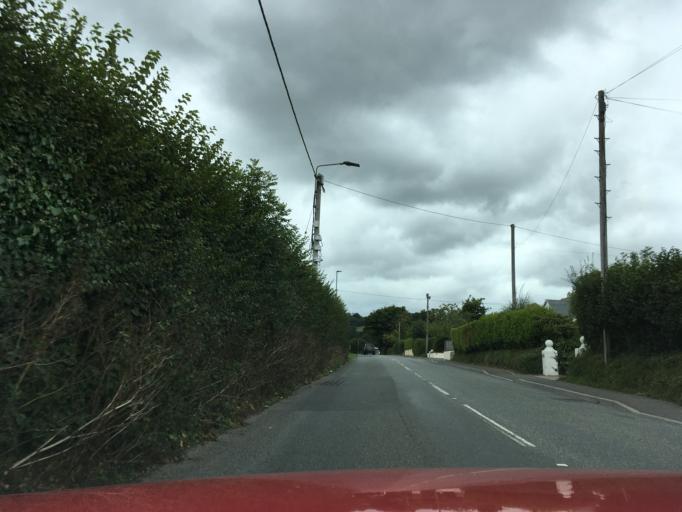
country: GB
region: England
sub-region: Devon
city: Bishopsteignton
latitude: 50.5484
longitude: -3.5440
